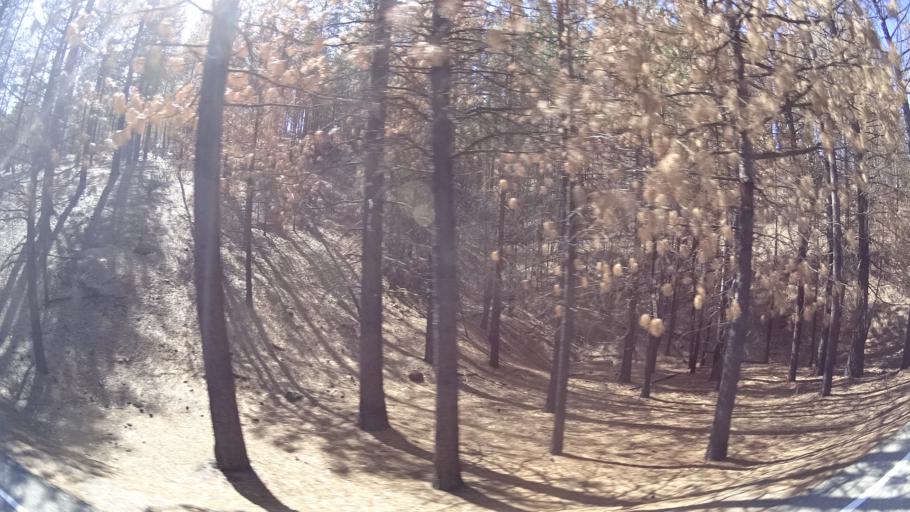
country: US
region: California
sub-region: Tehama County
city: Rancho Tehama Reserve
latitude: 39.6537
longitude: -122.7309
